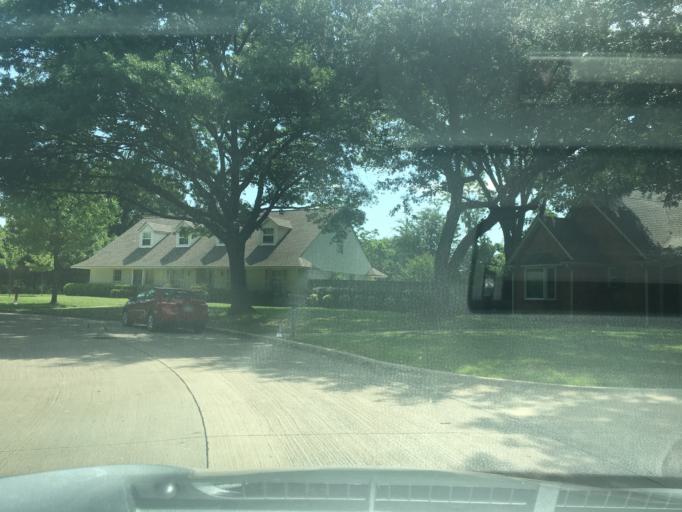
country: US
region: Texas
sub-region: Dallas County
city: Farmers Branch
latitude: 32.9300
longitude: -96.8586
